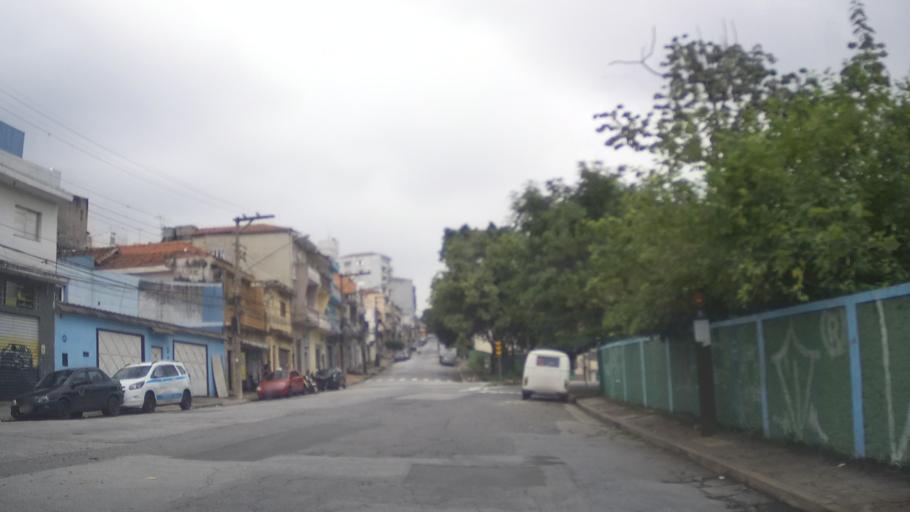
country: BR
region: Sao Paulo
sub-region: Sao Paulo
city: Sao Paulo
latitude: -23.5066
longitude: -46.5860
